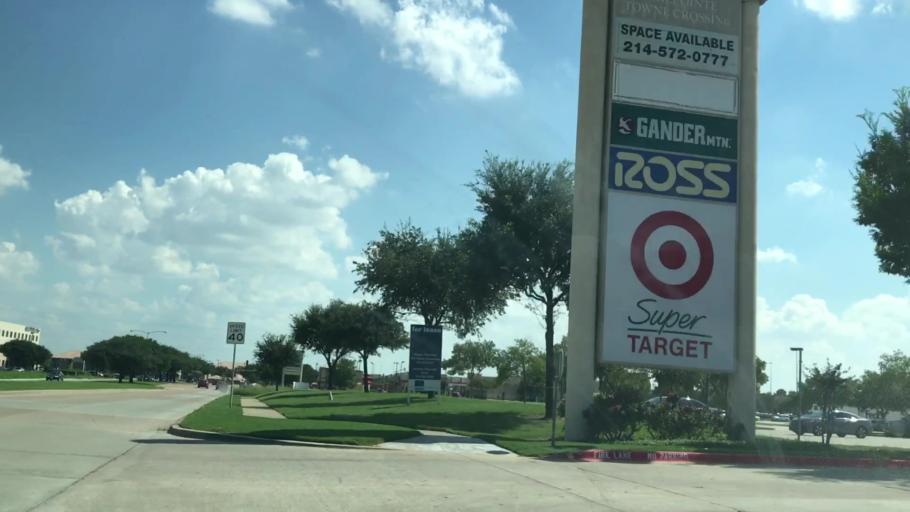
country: US
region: Texas
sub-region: Denton County
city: Lewisville
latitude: 33.0129
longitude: -96.9697
